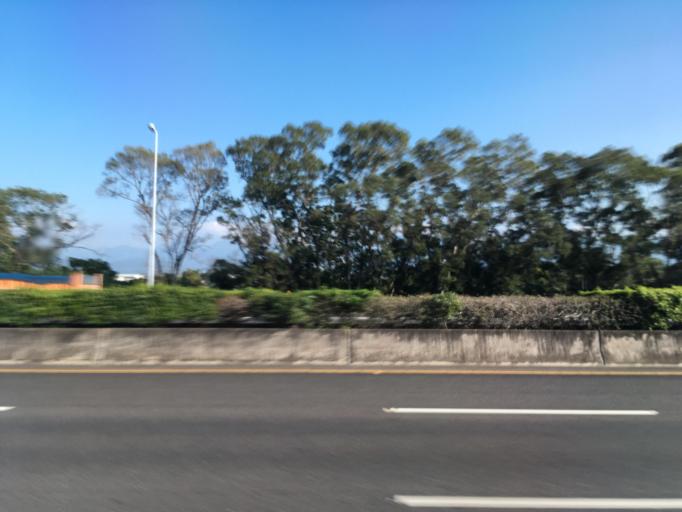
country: TW
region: Taiwan
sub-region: Chiayi
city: Jiayi Shi
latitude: 23.4463
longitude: 120.4827
